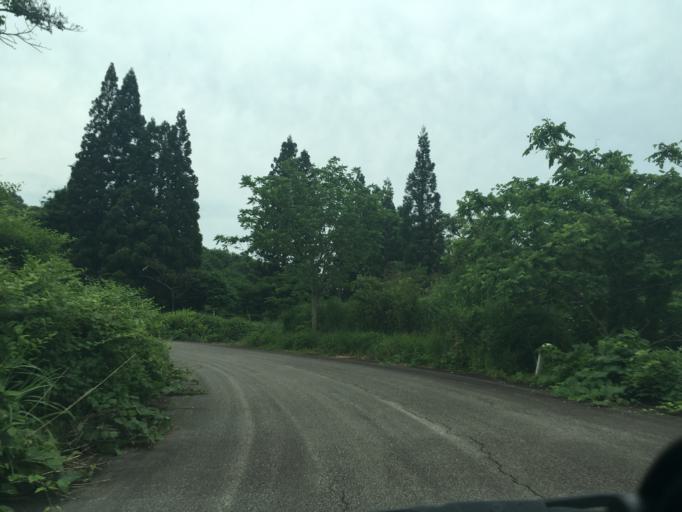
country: JP
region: Fukushima
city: Kitakata
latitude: 37.4694
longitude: 139.7633
